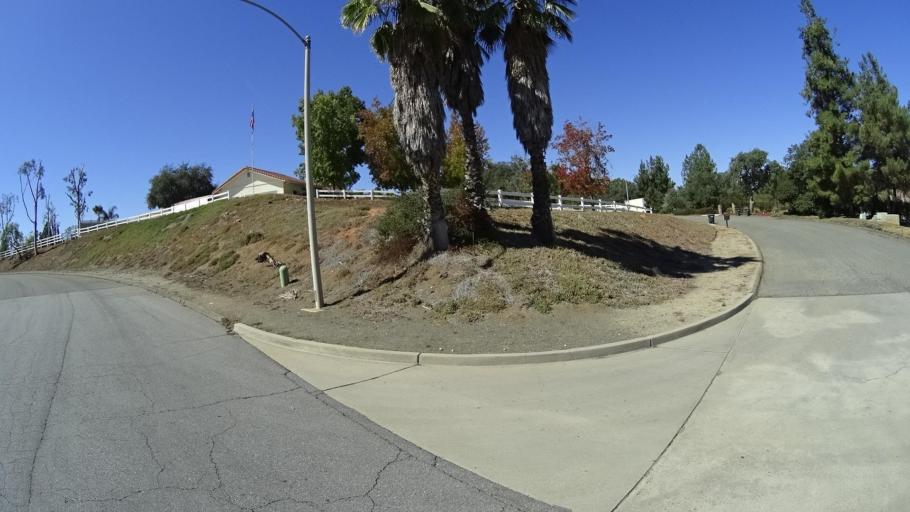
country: US
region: California
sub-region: San Diego County
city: Alpine
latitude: 32.8140
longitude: -116.7816
